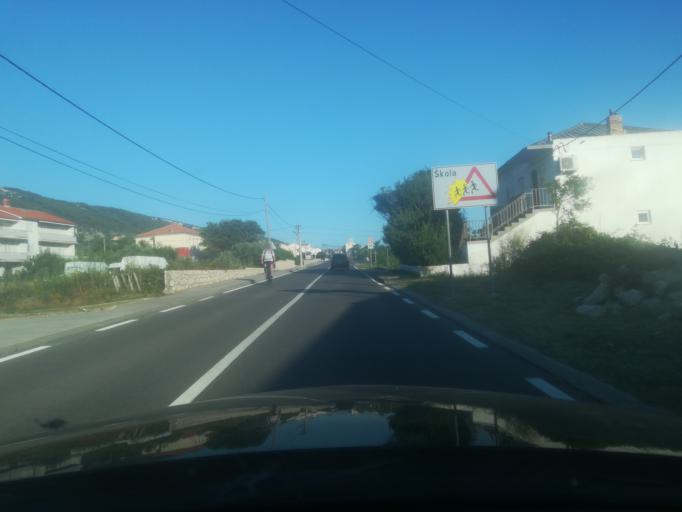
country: HR
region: Primorsko-Goranska
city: Banjol
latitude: 44.7729
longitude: 14.7598
